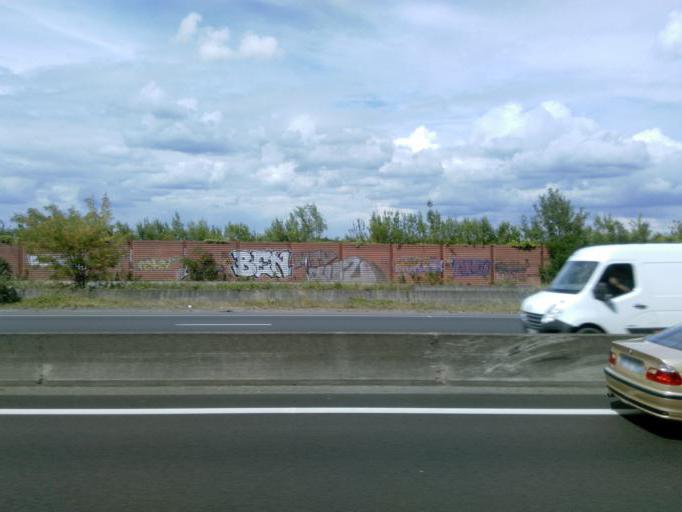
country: FR
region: Ile-de-France
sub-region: Departement du Val-d'Oise
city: Montigny-les-Cormeilles
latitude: 48.9870
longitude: 2.2089
